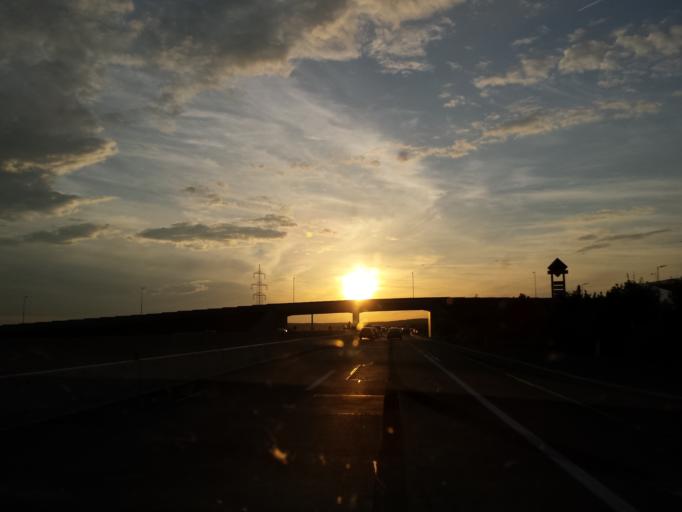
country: AT
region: Burgenland
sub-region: Politischer Bezirk Neusiedl am See
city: Parndorf
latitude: 47.9740
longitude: 16.8554
